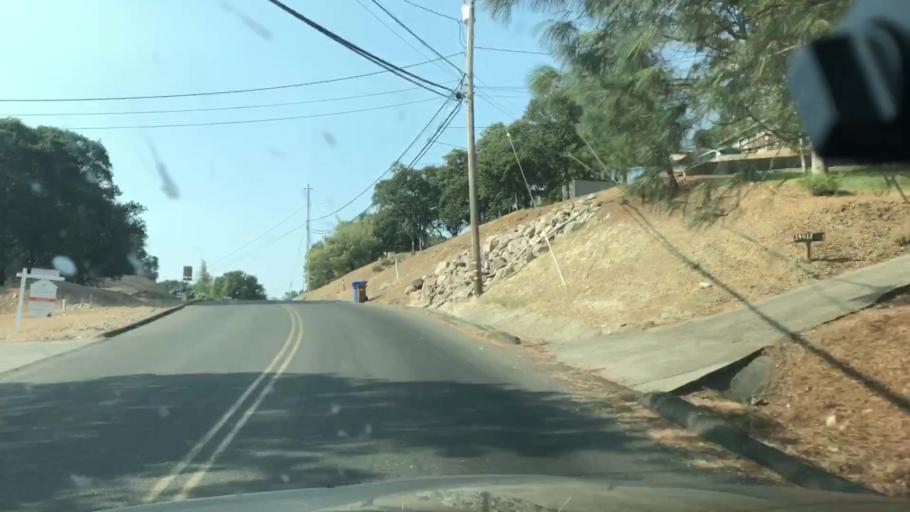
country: US
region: California
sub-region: Lake County
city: Hidden Valley Lake
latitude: 38.8047
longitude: -122.5589
